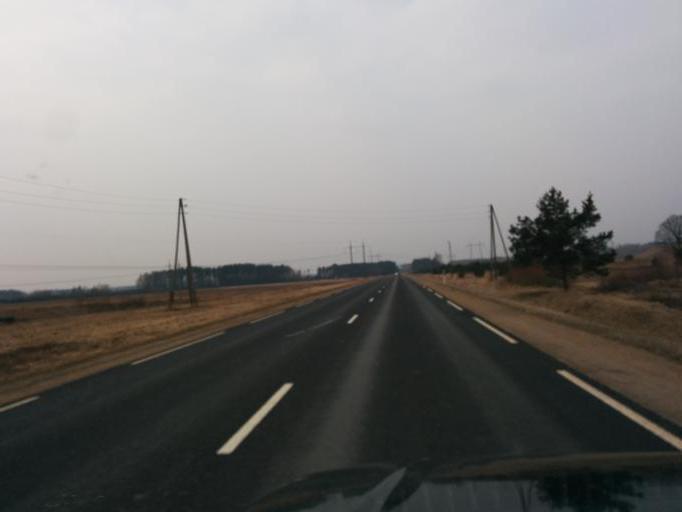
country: LV
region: Salaspils
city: Salaspils
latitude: 56.8219
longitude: 24.3040
